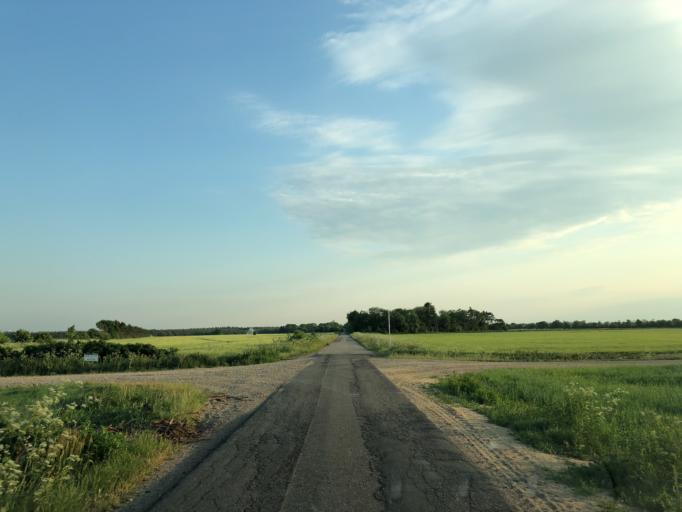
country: DK
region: Central Jutland
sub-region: Holstebro Kommune
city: Holstebro
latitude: 56.3822
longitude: 8.4652
